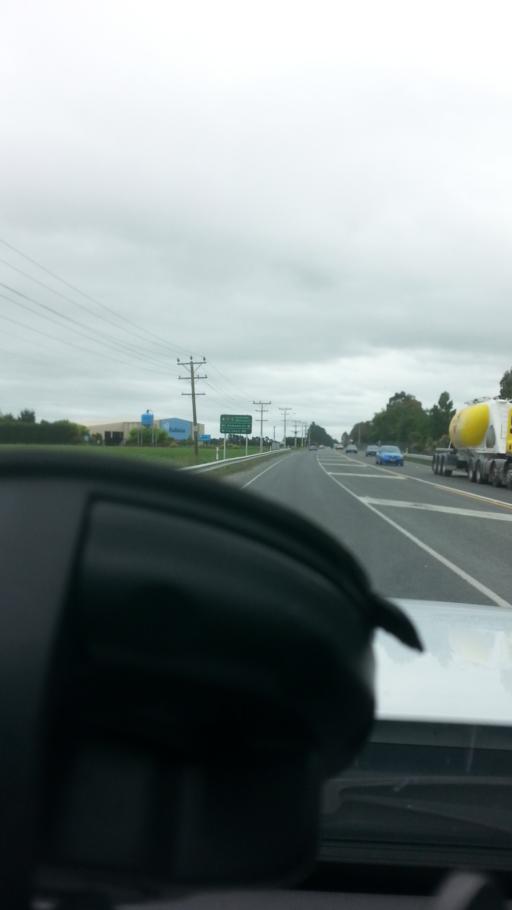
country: NZ
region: Wellington
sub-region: Masterton District
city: Masterton
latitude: -40.9668
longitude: 175.6060
